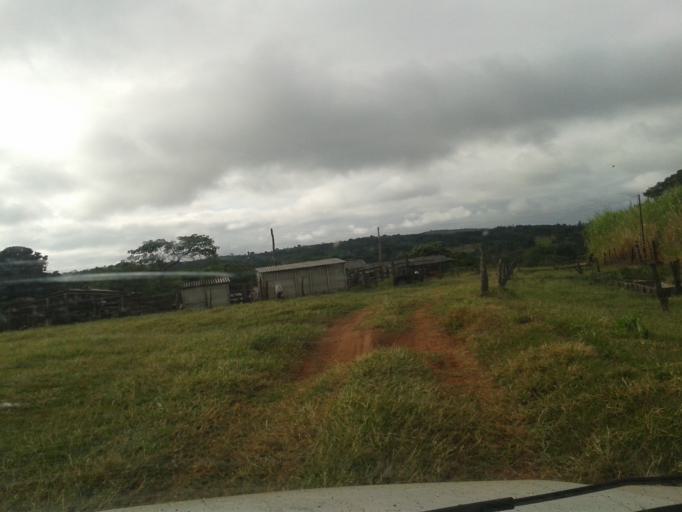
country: BR
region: Minas Gerais
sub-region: Campina Verde
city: Campina Verde
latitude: -19.4115
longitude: -49.6284
